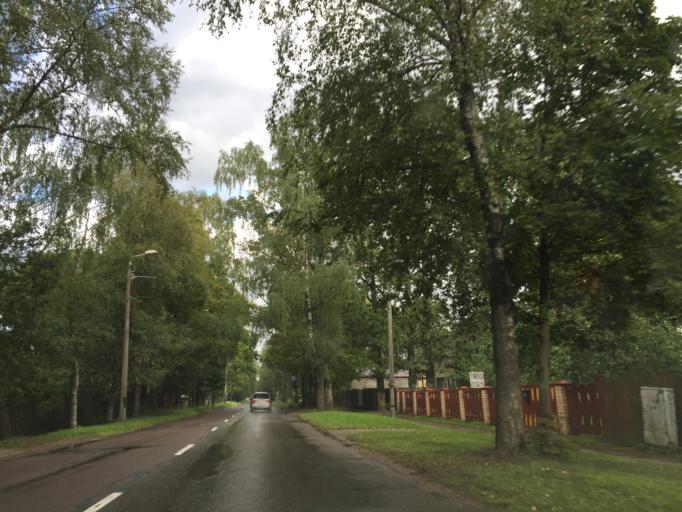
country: LV
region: Babite
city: Pinki
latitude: 56.9537
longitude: 23.9786
